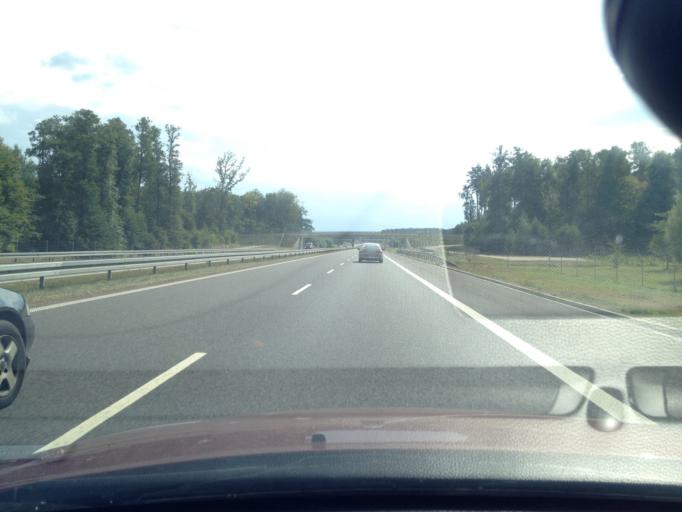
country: PL
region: West Pomeranian Voivodeship
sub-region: Powiat mysliborski
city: Mysliborz
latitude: 53.0153
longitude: 14.8616
